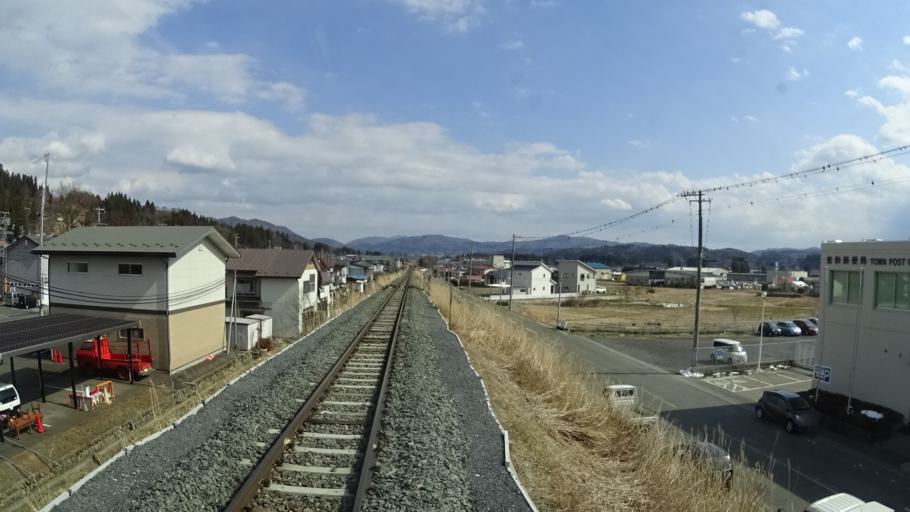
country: JP
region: Iwate
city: Hanamaki
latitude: 39.3864
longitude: 141.2278
